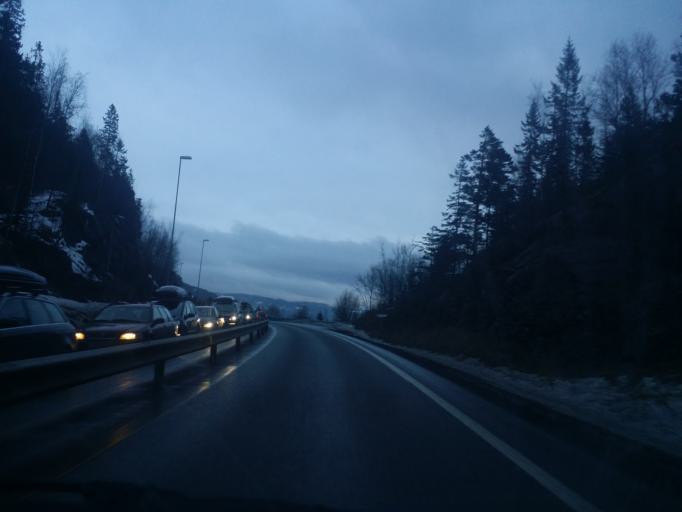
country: NO
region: Buskerud
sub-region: Hole
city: Vik
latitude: 60.0086
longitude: 10.2715
